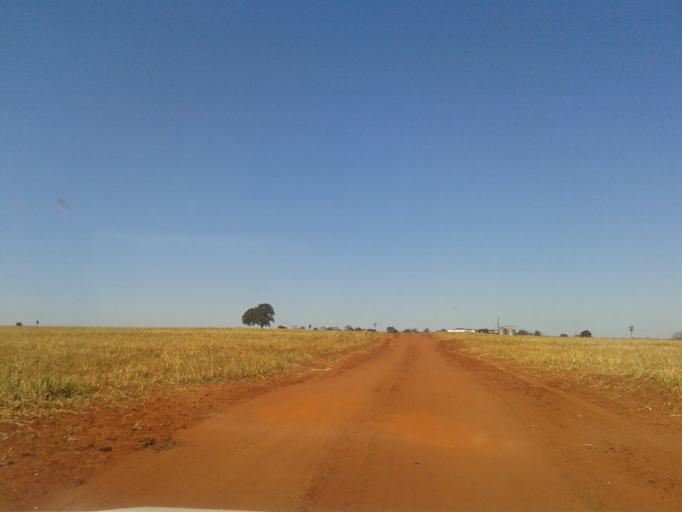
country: BR
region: Minas Gerais
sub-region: Santa Vitoria
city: Santa Vitoria
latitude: -19.2299
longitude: -50.2090
